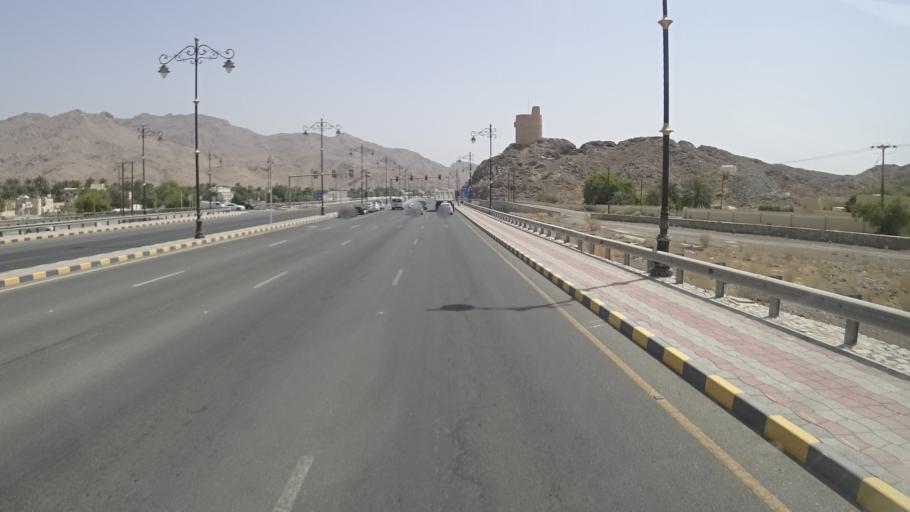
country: OM
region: Muhafazat ad Dakhiliyah
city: Nizwa
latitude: 22.9491
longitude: 57.5248
